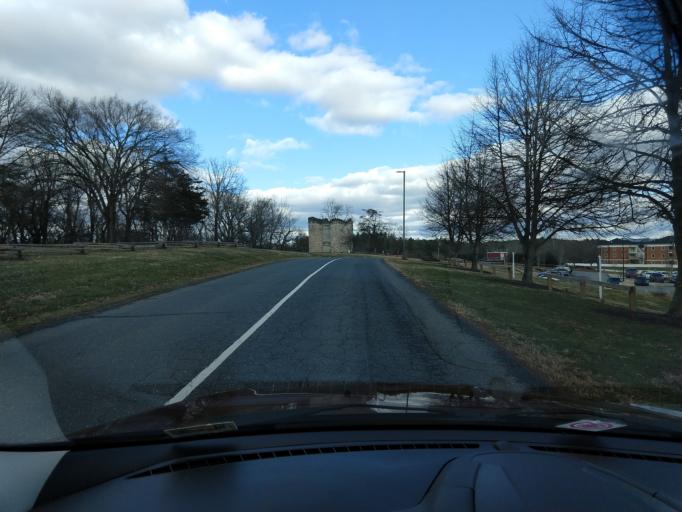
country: US
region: Virginia
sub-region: City of Lexington
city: Lexington
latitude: 37.7945
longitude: -79.4497
